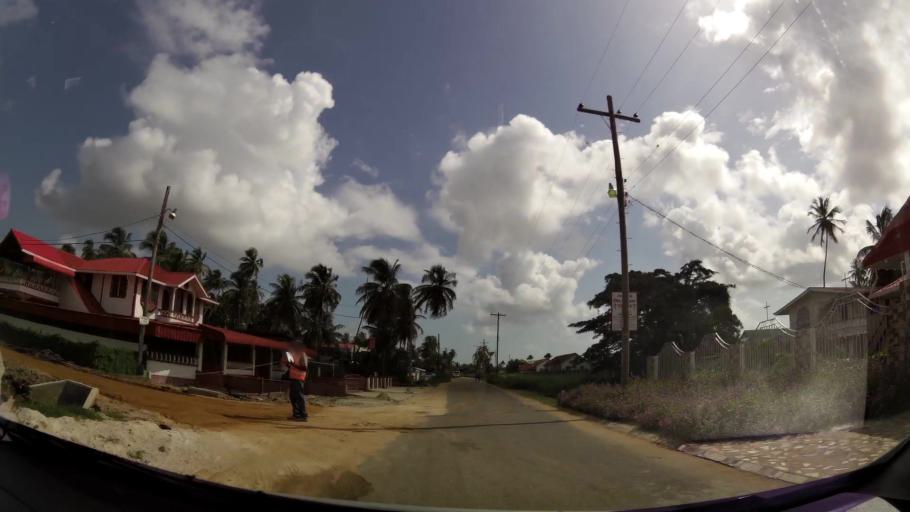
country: GY
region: Demerara-Mahaica
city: Mahaica Village
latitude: 6.7089
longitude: -57.9276
